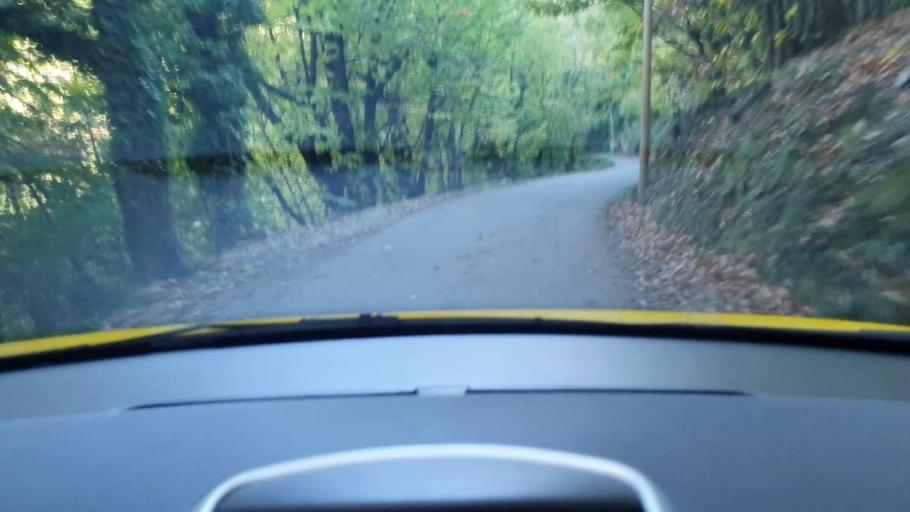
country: FR
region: Languedoc-Roussillon
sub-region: Departement du Gard
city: Sumene
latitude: 43.9924
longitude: 3.7509
